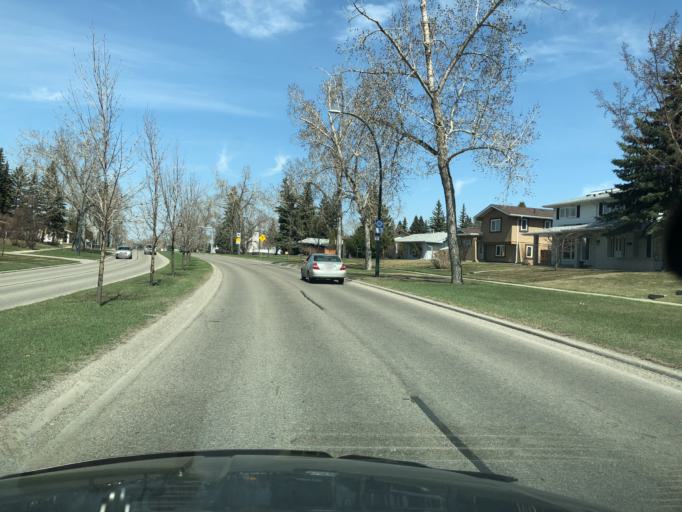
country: CA
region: Alberta
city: Calgary
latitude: 50.9436
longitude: -114.0428
